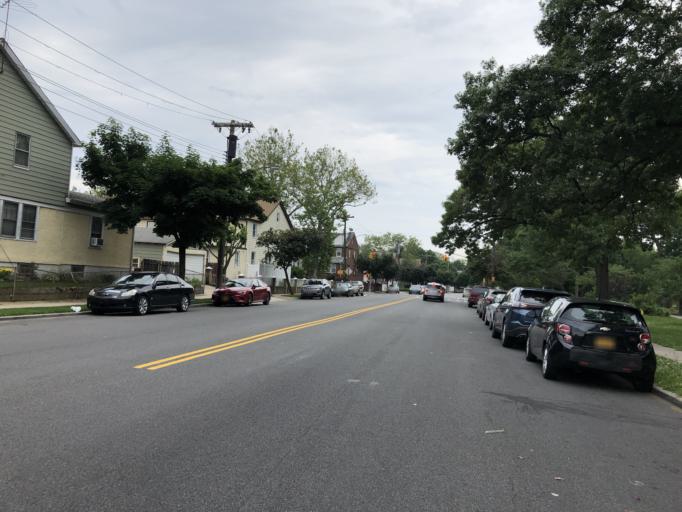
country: US
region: New York
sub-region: Nassau County
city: South Valley Stream
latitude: 40.6622
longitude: -73.7416
